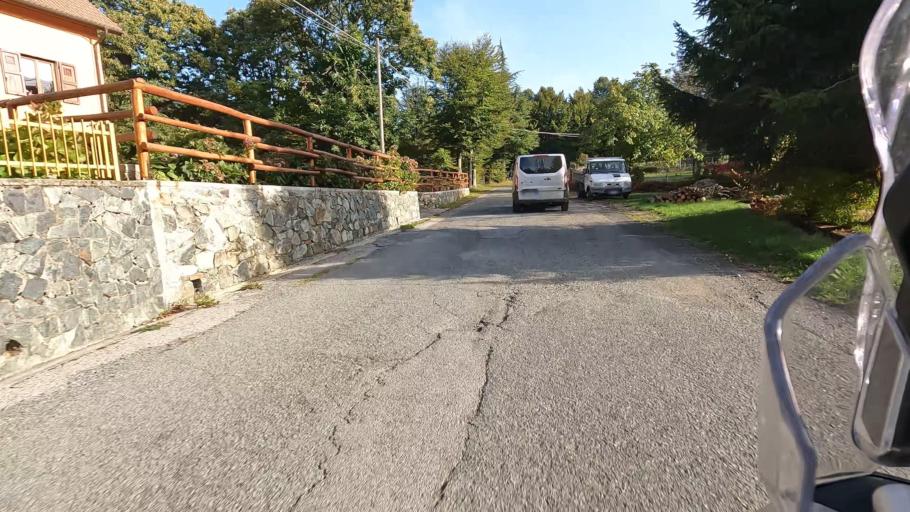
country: IT
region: Liguria
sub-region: Provincia di Savona
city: Urbe
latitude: 44.4585
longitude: 8.5810
